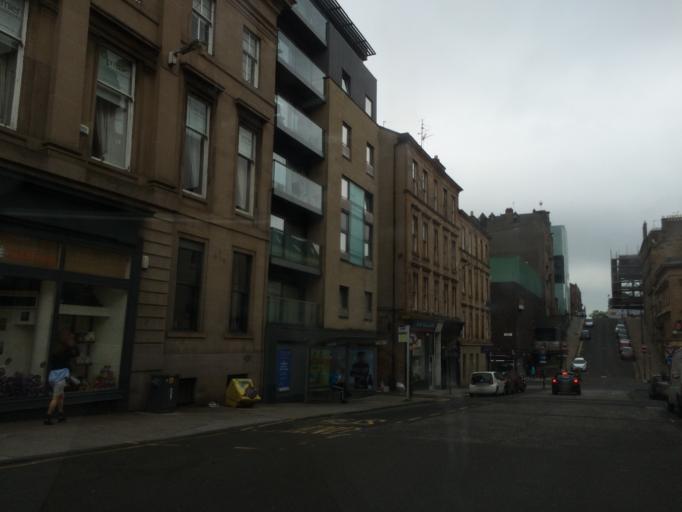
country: GB
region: Scotland
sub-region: Glasgow City
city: Glasgow
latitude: 55.8648
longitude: -4.2634
